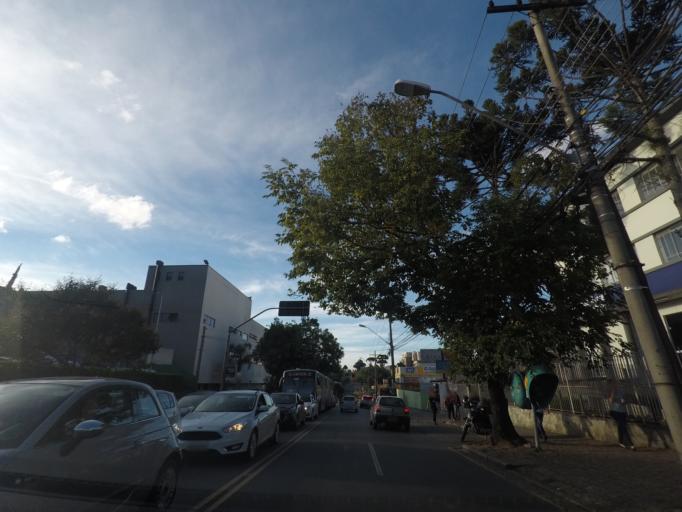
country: BR
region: Parana
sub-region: Curitiba
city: Curitiba
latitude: -25.4214
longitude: -49.2915
